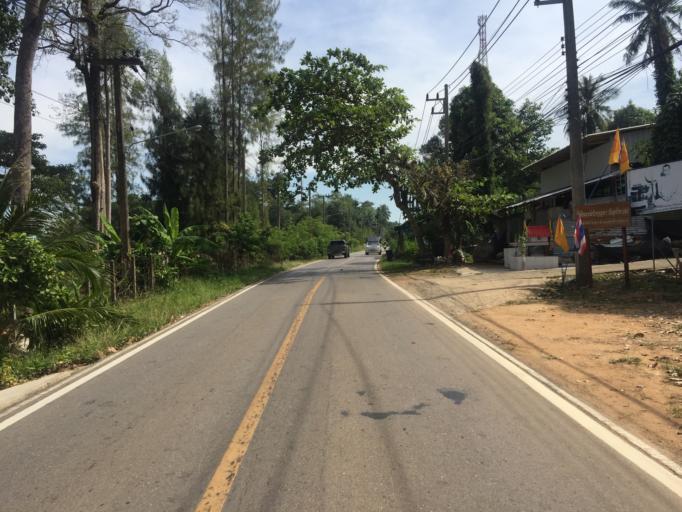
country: TH
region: Trat
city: Laem Ngop
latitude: 12.1391
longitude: 102.3072
